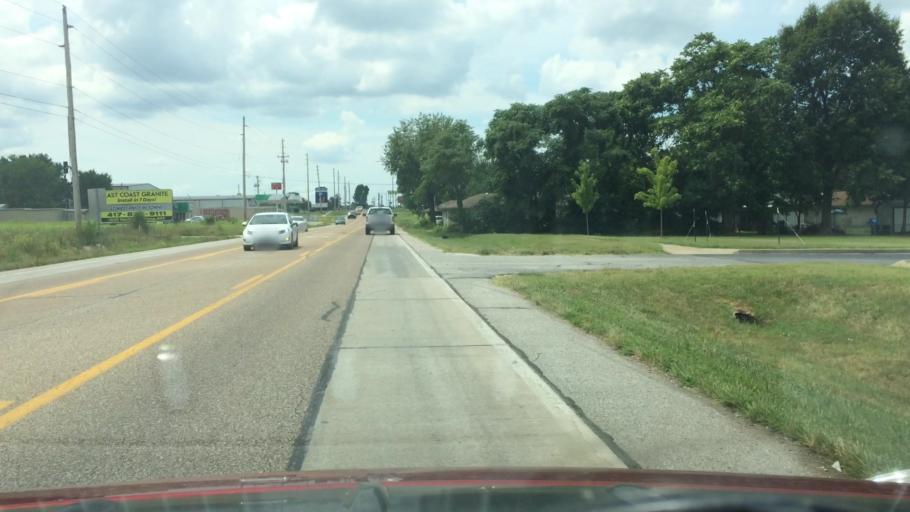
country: US
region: Missouri
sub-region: Greene County
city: Springfield
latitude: 37.2592
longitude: -93.2650
